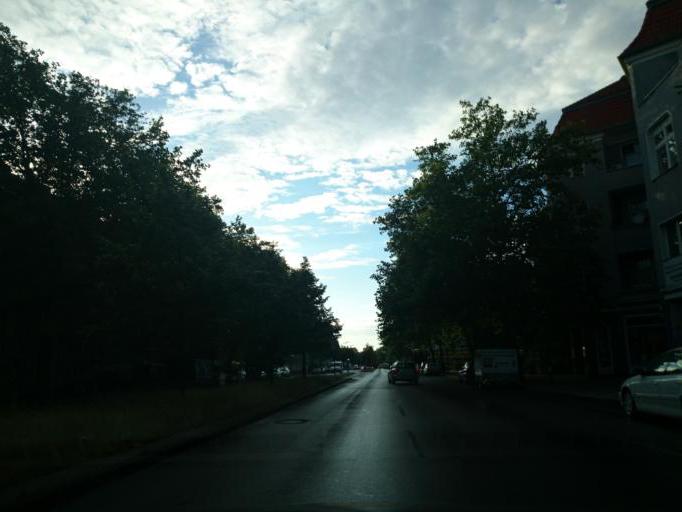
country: DE
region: Berlin
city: Wedding Bezirk
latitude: 52.5591
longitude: 13.3708
